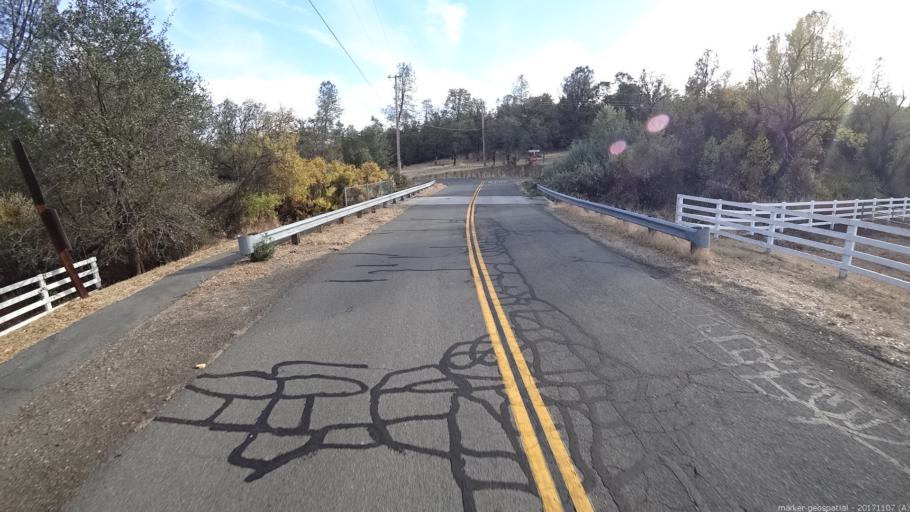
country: US
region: California
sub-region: Shasta County
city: Shasta
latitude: 40.5192
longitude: -122.4595
